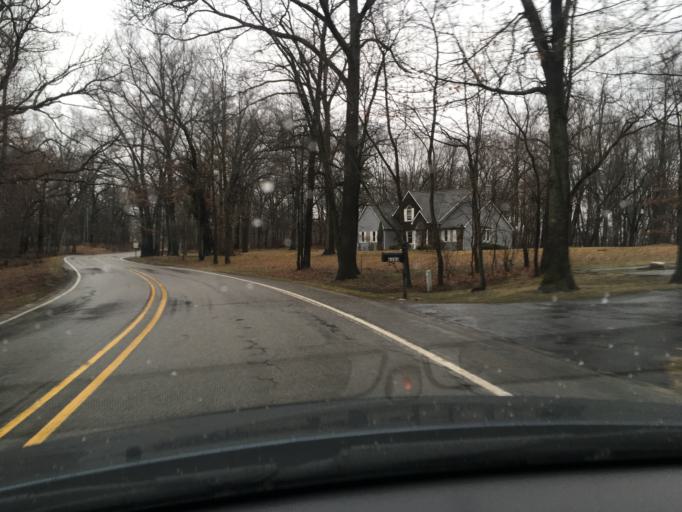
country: US
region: Michigan
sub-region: Jackson County
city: Grass Lake
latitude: 42.3310
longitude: -84.1545
